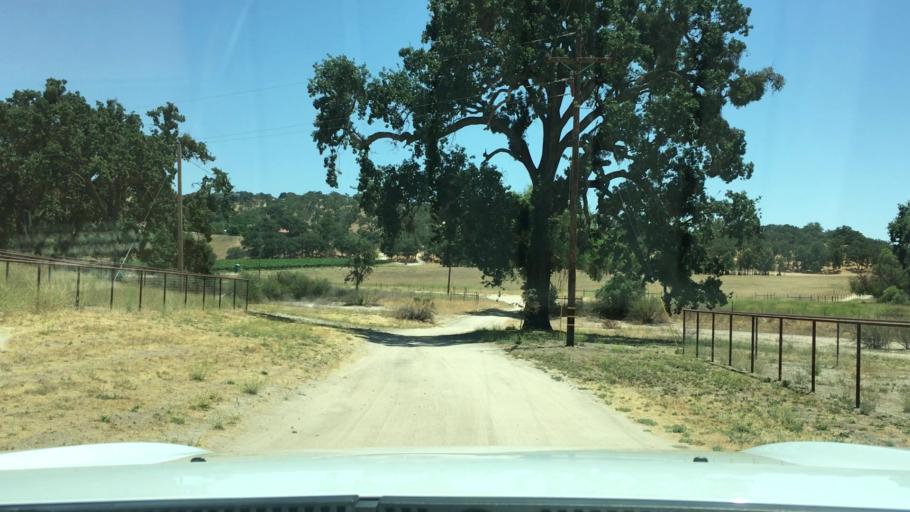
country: US
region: California
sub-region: San Luis Obispo County
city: Paso Robles
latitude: 35.5966
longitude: -120.6035
